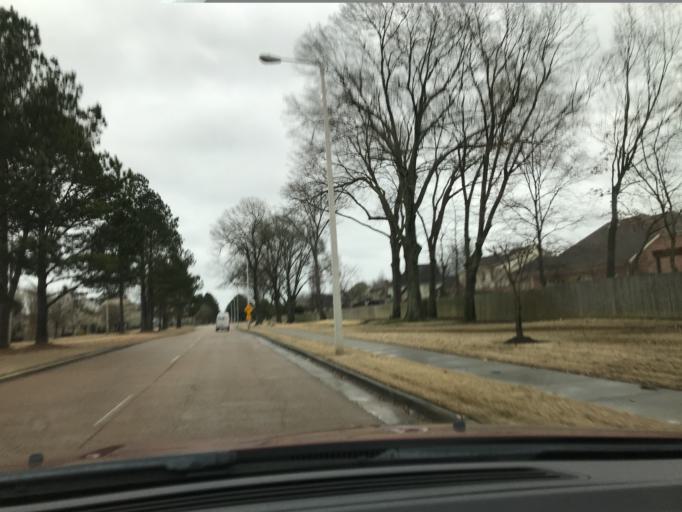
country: US
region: Tennessee
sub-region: Shelby County
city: Collierville
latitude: 35.0855
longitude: -89.6980
